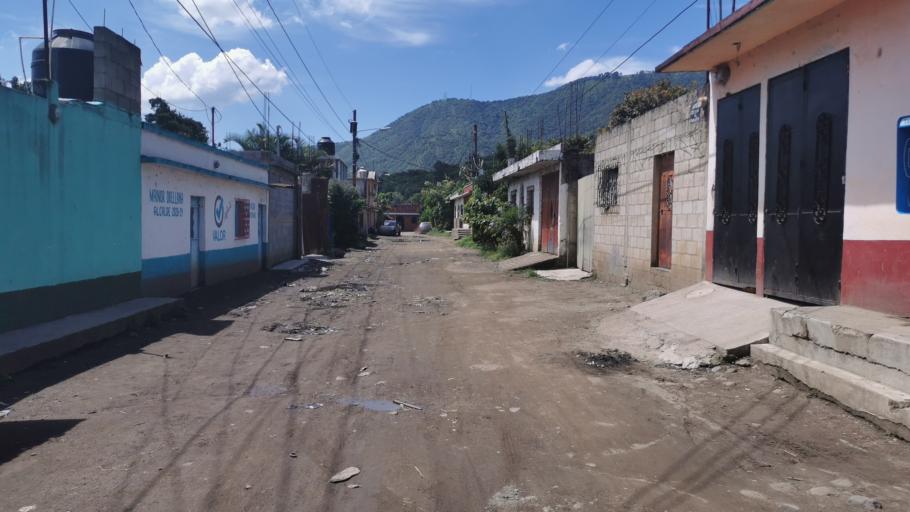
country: GT
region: Guatemala
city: Amatitlan
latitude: 14.4864
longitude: -90.6403
